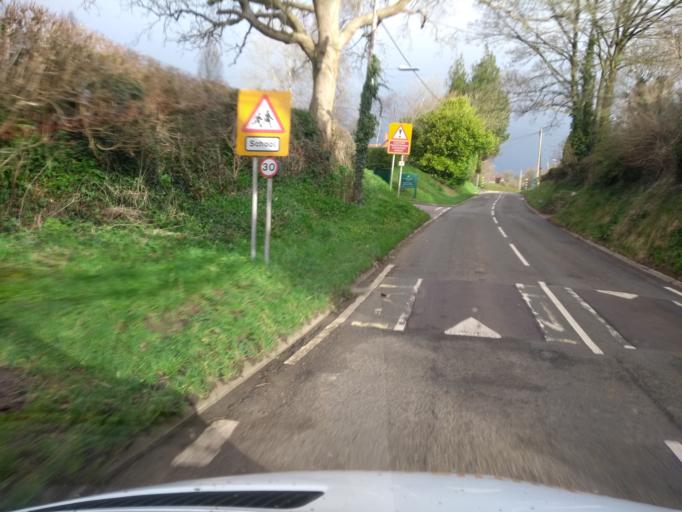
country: GB
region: England
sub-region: Somerset
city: Bruton
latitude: 51.0984
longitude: -2.4666
